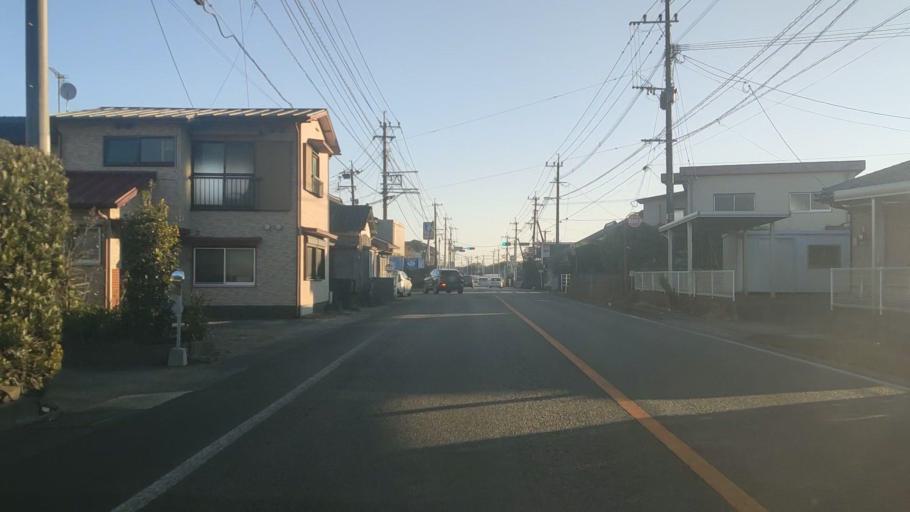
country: JP
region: Miyazaki
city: Takanabe
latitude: 32.0763
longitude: 131.5027
